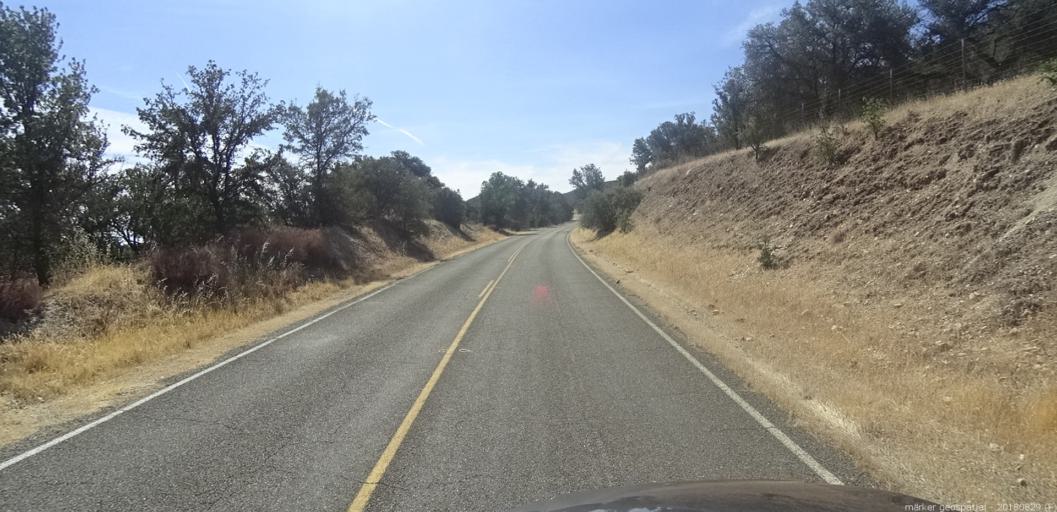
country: US
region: California
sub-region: San Luis Obispo County
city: Lake Nacimiento
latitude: 35.8945
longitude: -121.0845
